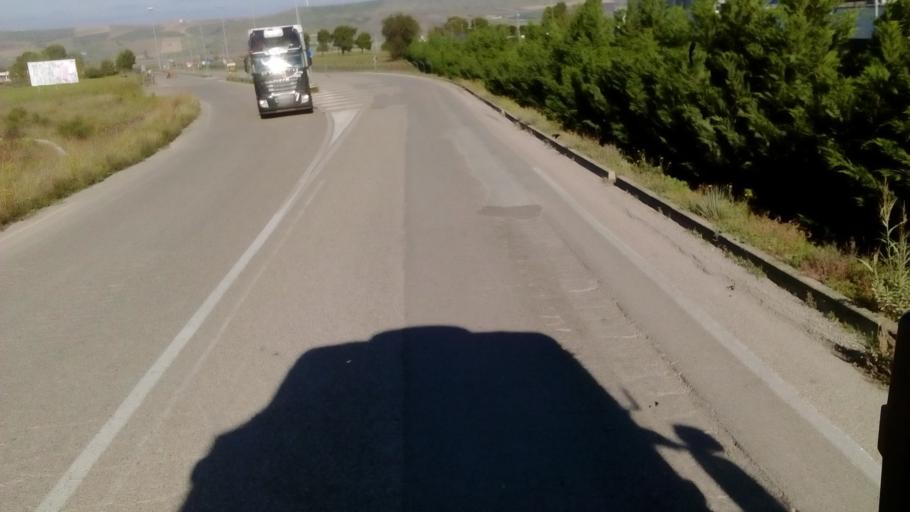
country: IT
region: Basilicate
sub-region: Provincia di Potenza
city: Melfi
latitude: 41.0744
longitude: 15.6917
